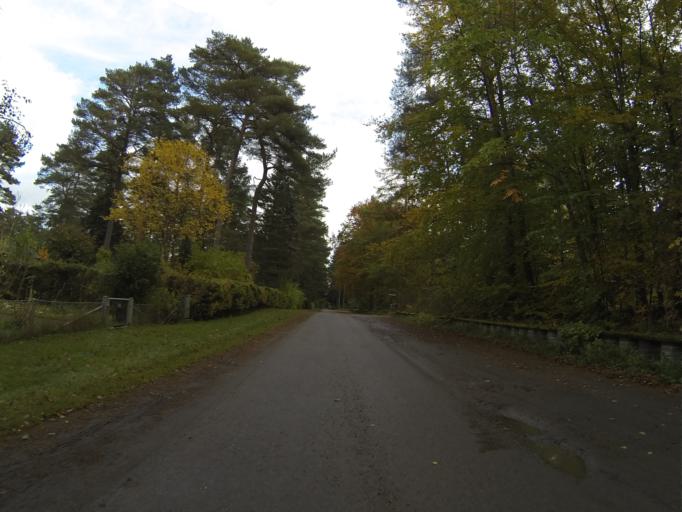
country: SE
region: Skane
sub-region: Sjobo Kommun
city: Sjoebo
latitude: 55.6326
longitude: 13.6605
